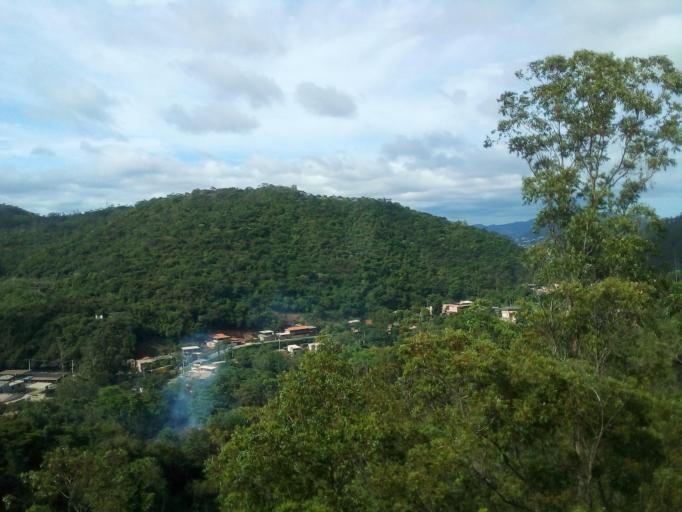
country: BR
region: Minas Gerais
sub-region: Raposos
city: Raposos
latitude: -19.8718
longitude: -43.7863
